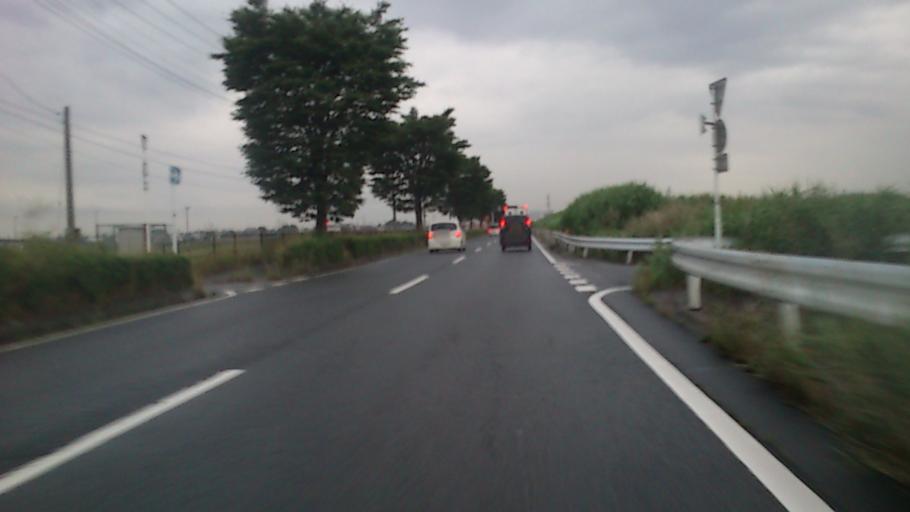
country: JP
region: Saitama
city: Gyoda
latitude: 36.1468
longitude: 139.4247
